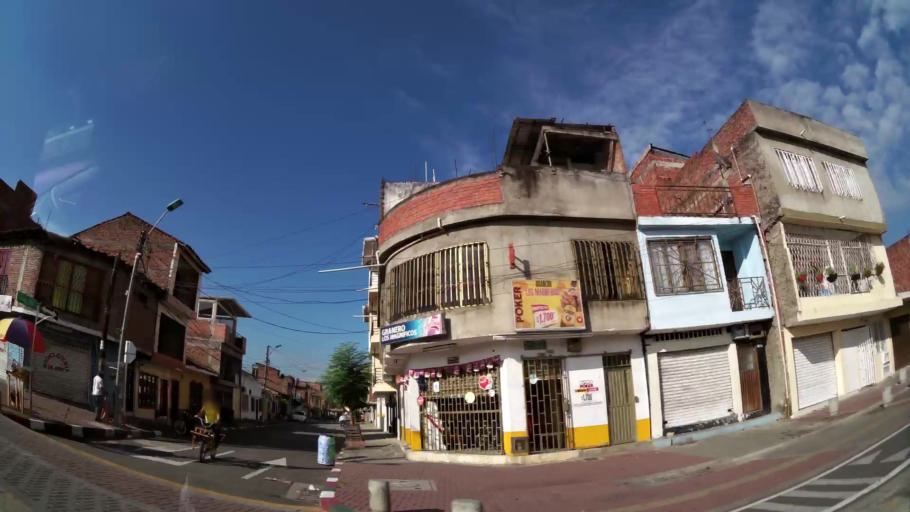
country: CO
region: Valle del Cauca
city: Cali
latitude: 3.4293
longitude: -76.5069
